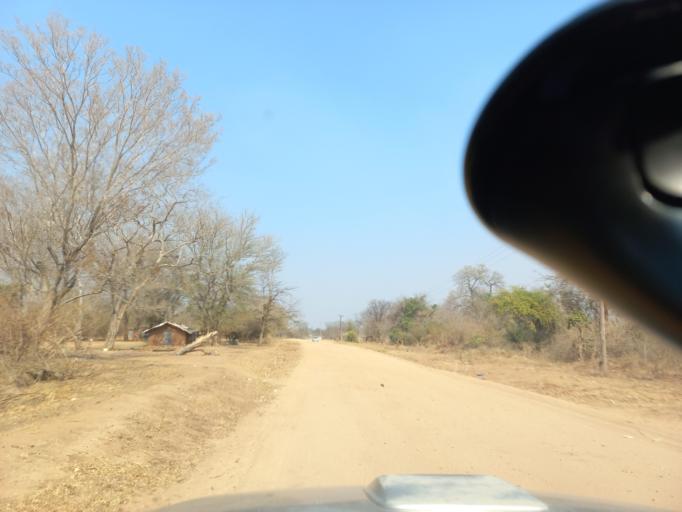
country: ZW
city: Chirundu
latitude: -15.9370
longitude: 28.9100
